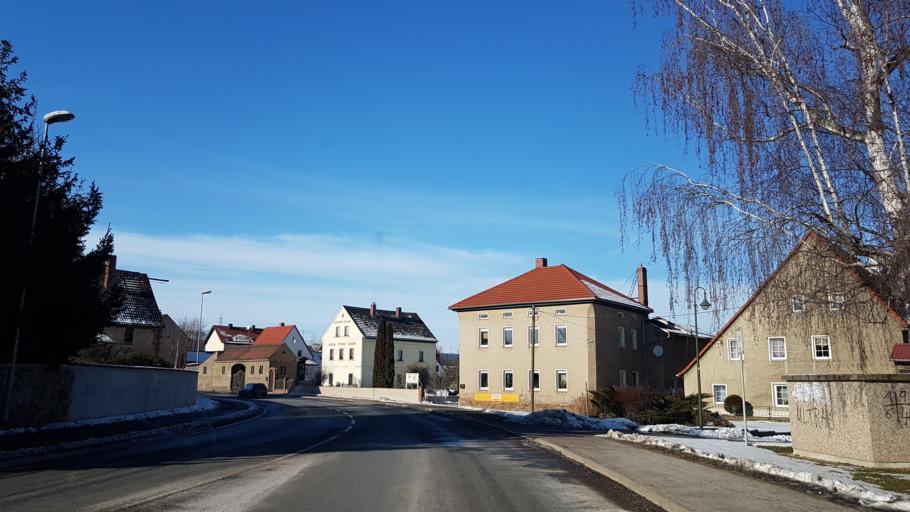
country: DE
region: Thuringia
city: Nobitz
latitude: 50.9839
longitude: 12.4749
